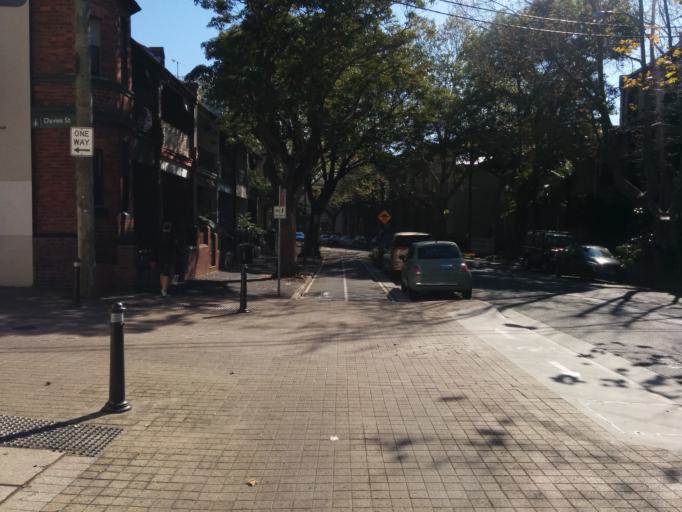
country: AU
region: New South Wales
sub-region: City of Sydney
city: Darlinghurst
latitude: -33.8887
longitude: 151.2153
